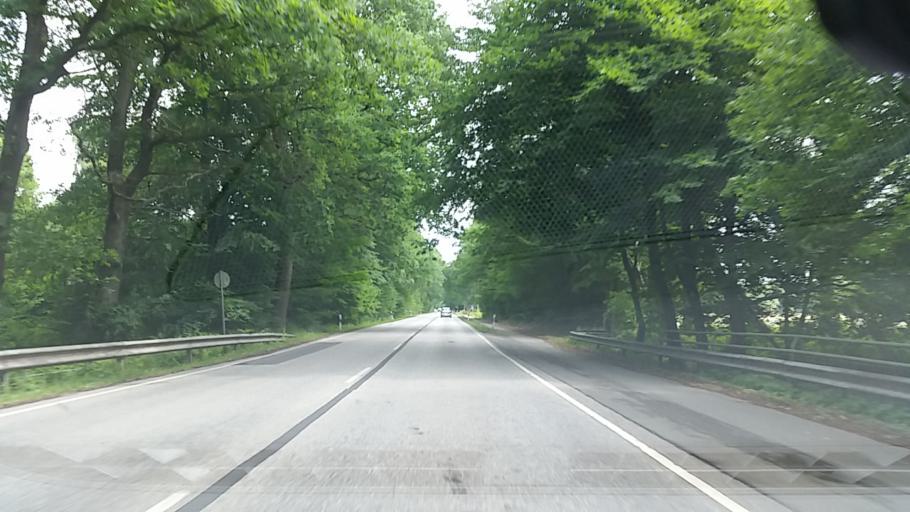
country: DE
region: Hamburg
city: Duvenstedt
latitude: 53.7365
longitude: 10.1138
